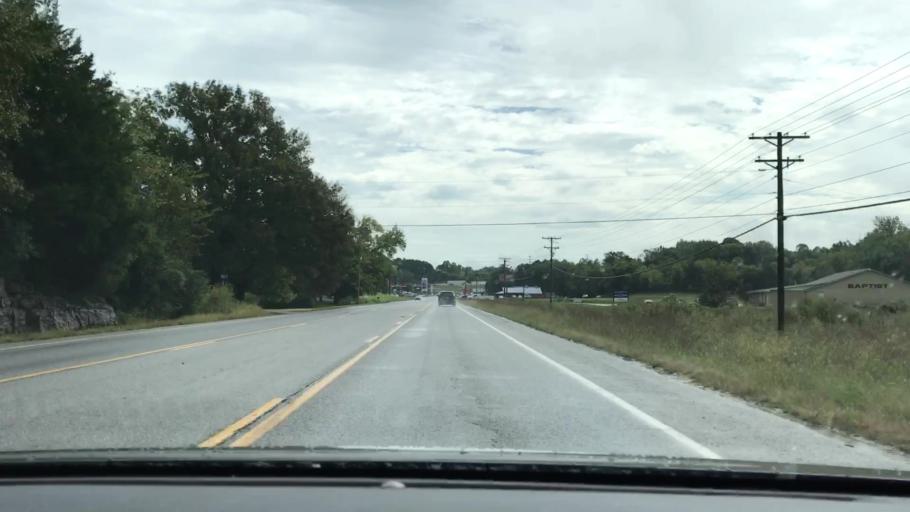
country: US
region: Tennessee
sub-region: Smith County
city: Gordonsville
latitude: 36.1854
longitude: -85.9501
